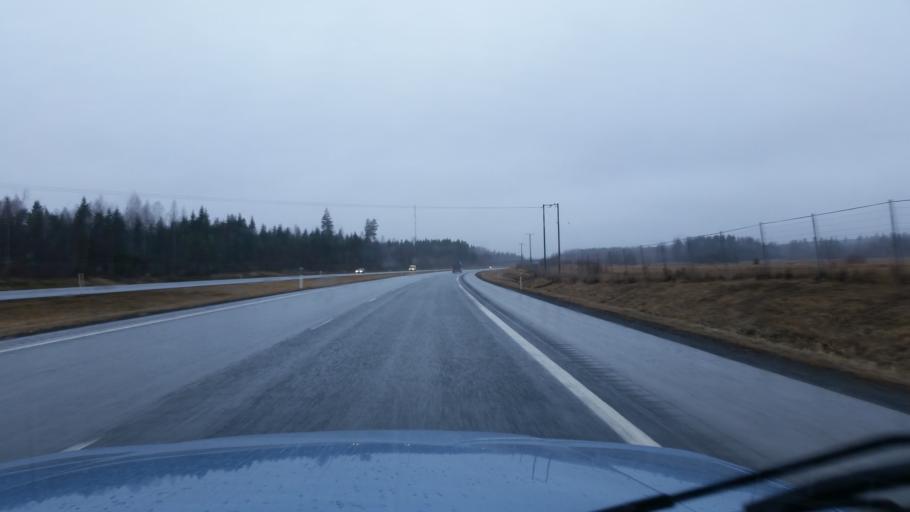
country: FI
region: Haeme
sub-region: Haemeenlinna
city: Kalvola
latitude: 61.1445
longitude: 24.0108
